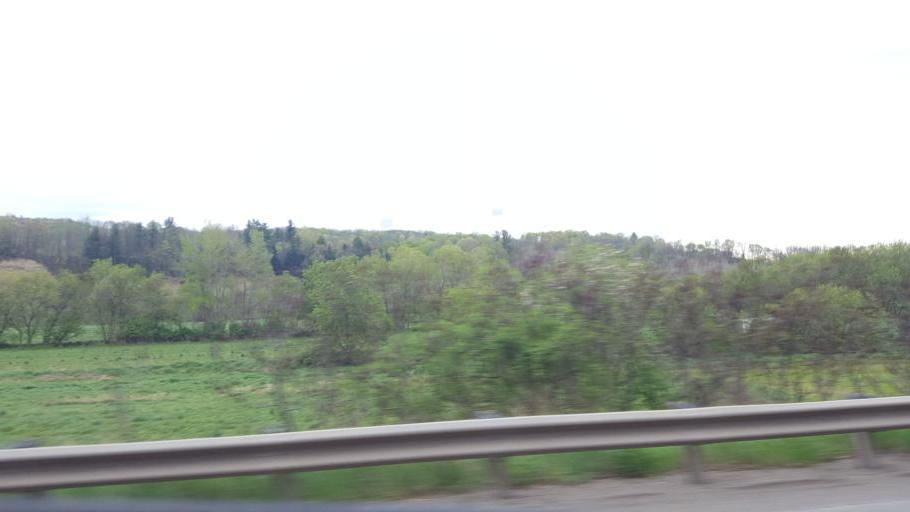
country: US
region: Pennsylvania
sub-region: Tioga County
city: Westfield
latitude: 41.9417
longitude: -77.4789
